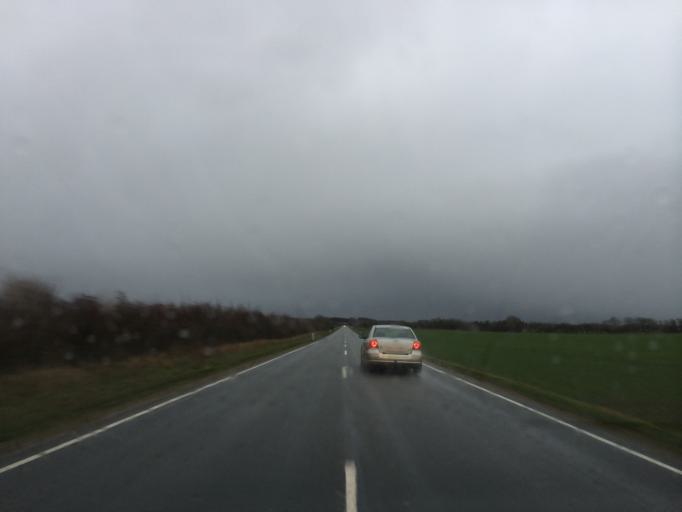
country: DK
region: South Denmark
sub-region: Varde Kommune
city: Varde
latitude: 55.7148
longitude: 8.4942
